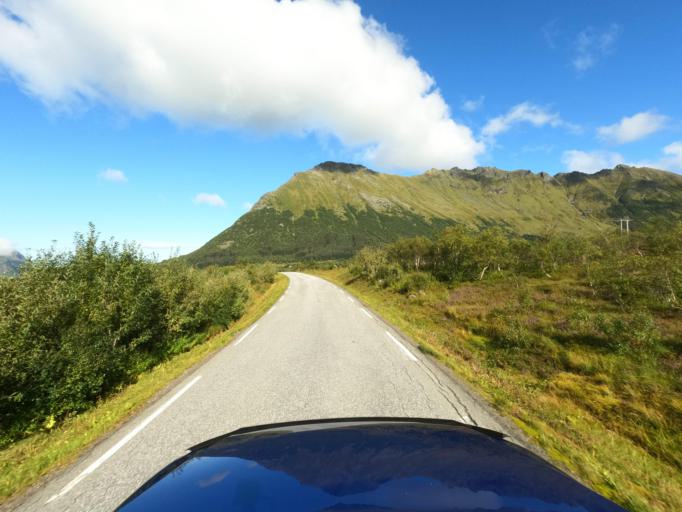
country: NO
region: Nordland
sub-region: Vagan
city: Kabelvag
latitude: 68.2808
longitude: 14.3519
